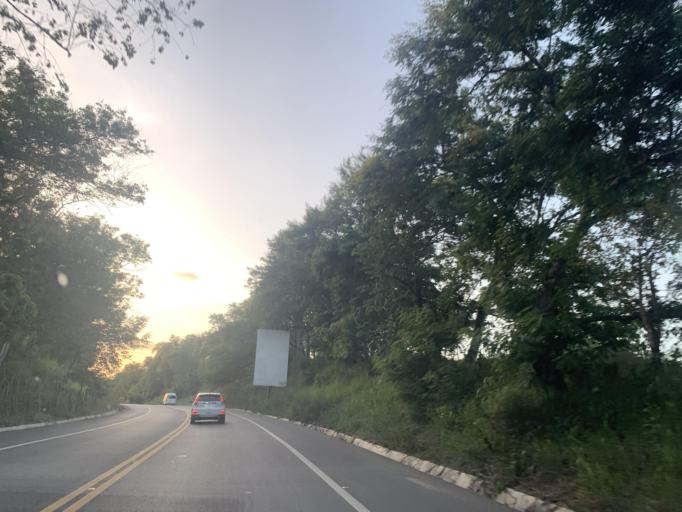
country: DO
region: Puerto Plata
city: Imbert
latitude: 19.7680
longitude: -70.8364
